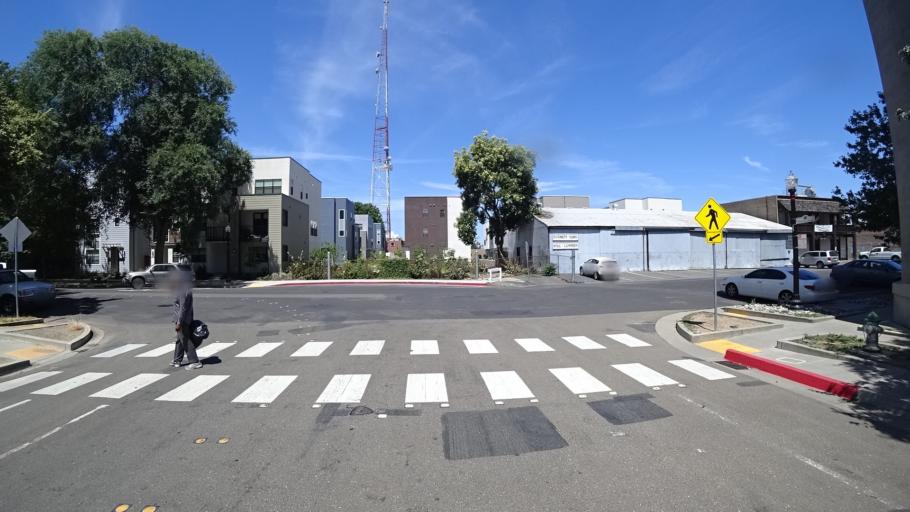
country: US
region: California
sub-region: Sacramento County
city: Sacramento
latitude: 38.5876
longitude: -121.4887
